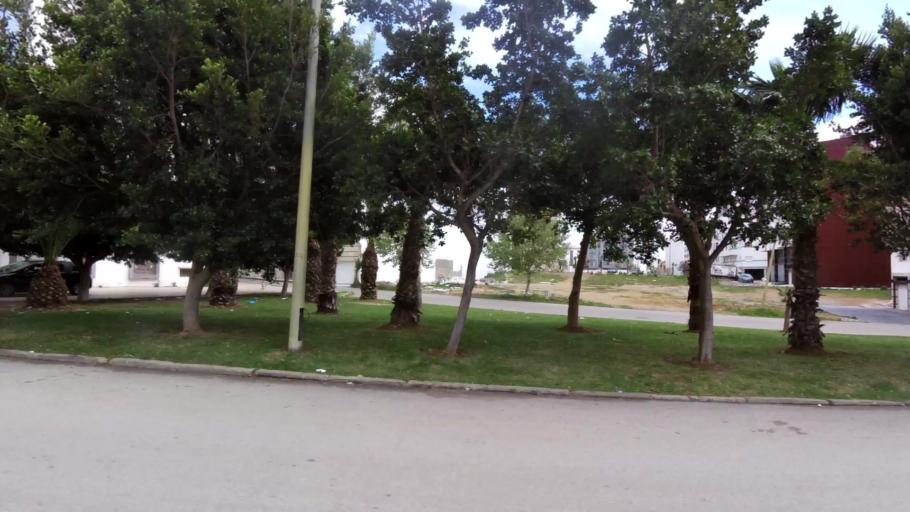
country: MA
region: Tanger-Tetouan
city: Tetouan
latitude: 35.5883
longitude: -5.3416
